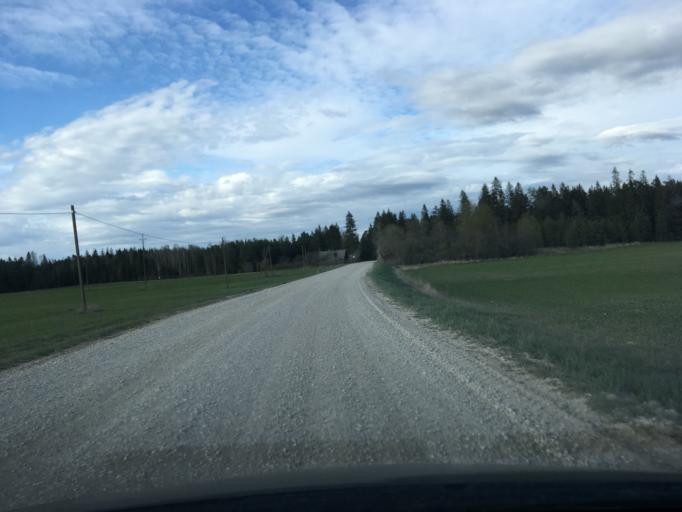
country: EE
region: Raplamaa
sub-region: Maerjamaa vald
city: Marjamaa
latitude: 58.9487
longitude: 24.3200
